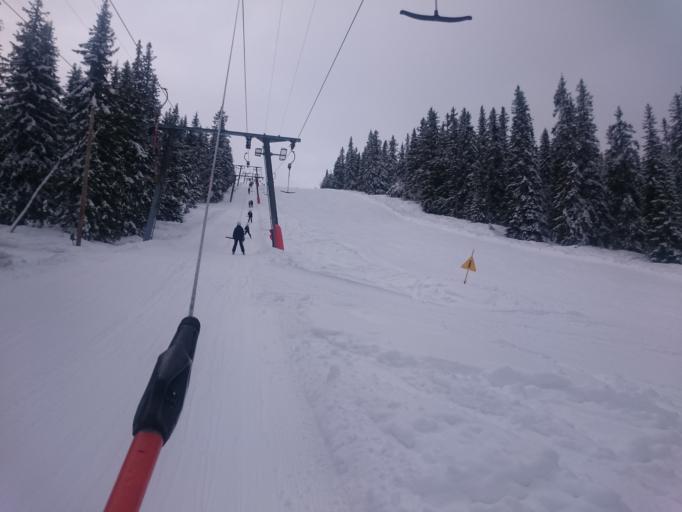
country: SE
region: Dalarna
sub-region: Malung-Saelens kommun
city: Malung
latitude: 61.1635
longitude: 13.1696
